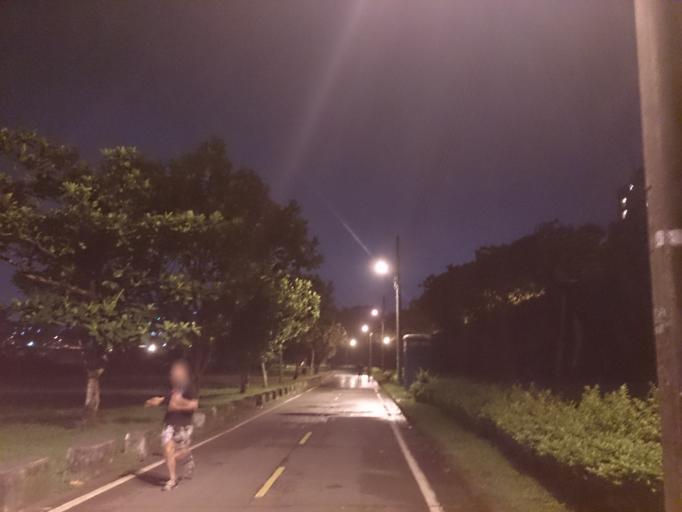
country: TW
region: Taipei
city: Taipei
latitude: 24.9917
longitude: 121.5371
